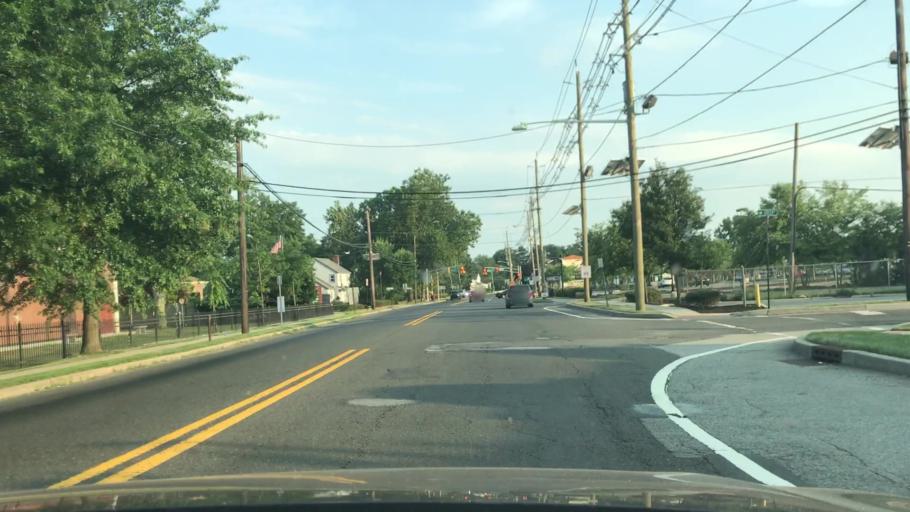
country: US
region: New Jersey
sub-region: Bergen County
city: Emerson
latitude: 40.9831
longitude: -74.0245
